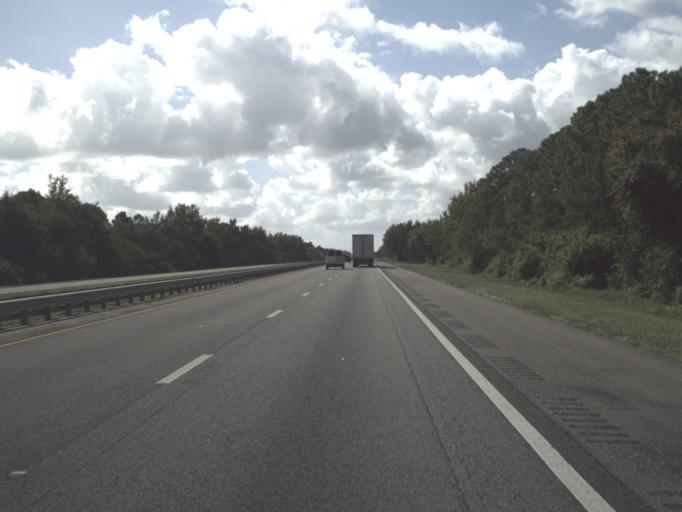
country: US
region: Florida
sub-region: Brevard County
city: June Park
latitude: 27.8486
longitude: -81.0076
